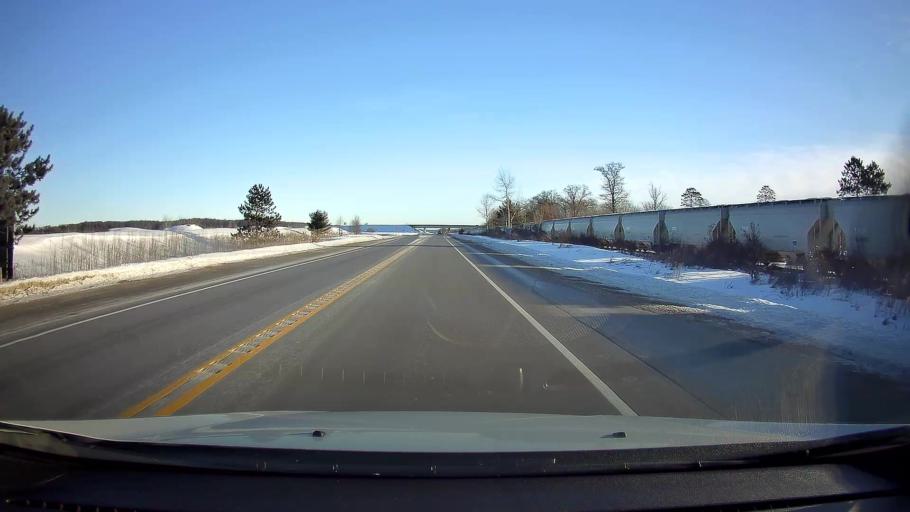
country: US
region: Wisconsin
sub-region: Washburn County
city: Spooner
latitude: 45.8492
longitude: -91.8645
